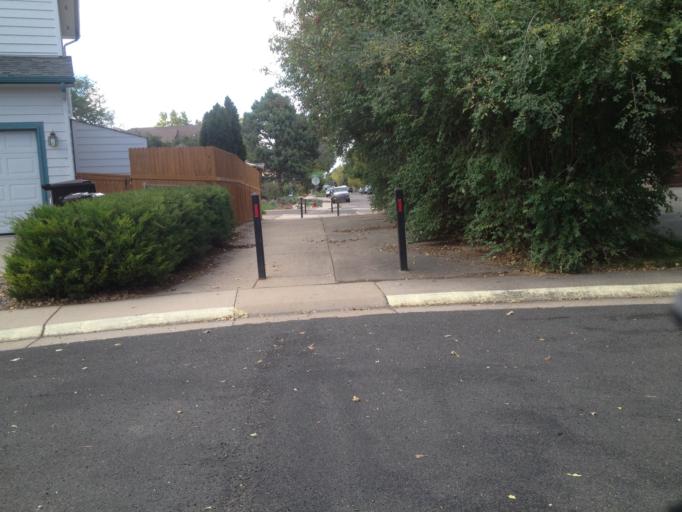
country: US
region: Colorado
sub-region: Boulder County
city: Louisville
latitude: 39.9743
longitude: -105.1370
